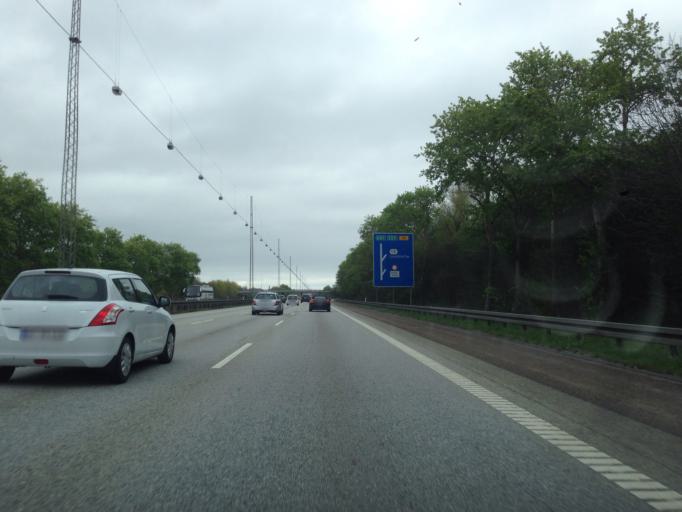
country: DK
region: Capital Region
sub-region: Lyngby-Tarbaek Kommune
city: Kongens Lyngby
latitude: 55.7839
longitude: 12.5278
